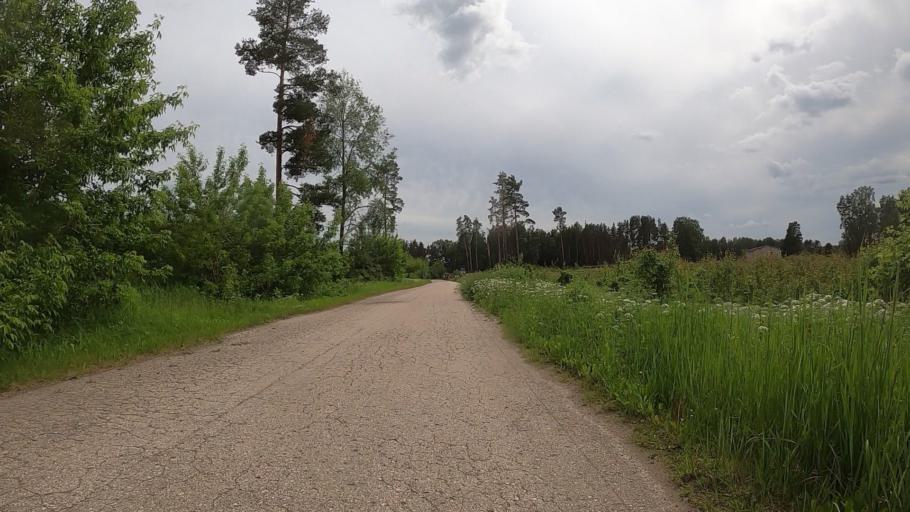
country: LV
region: Olaine
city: Olaine
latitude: 56.8037
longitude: 23.9242
